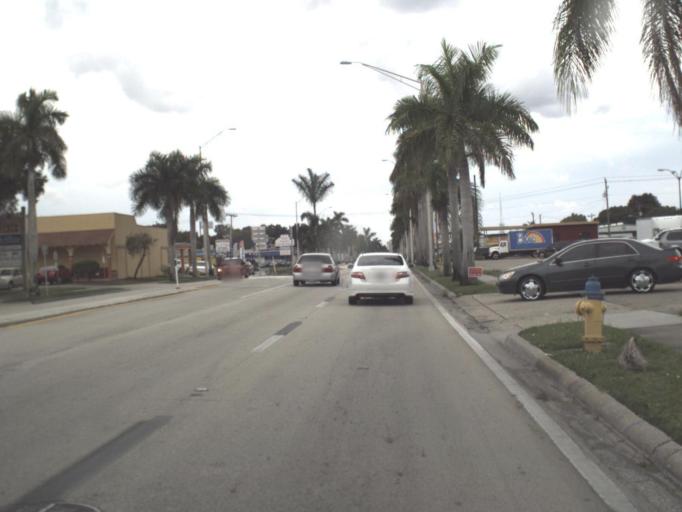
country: US
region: Florida
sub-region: Lee County
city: Tice
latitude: 26.6661
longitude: -81.8310
